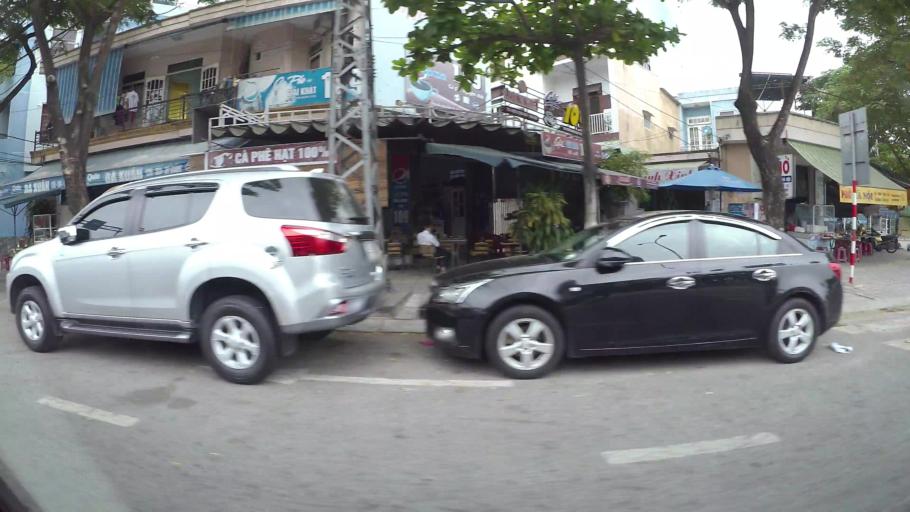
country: VN
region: Da Nang
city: Da Nang
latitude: 16.0515
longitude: 108.2092
